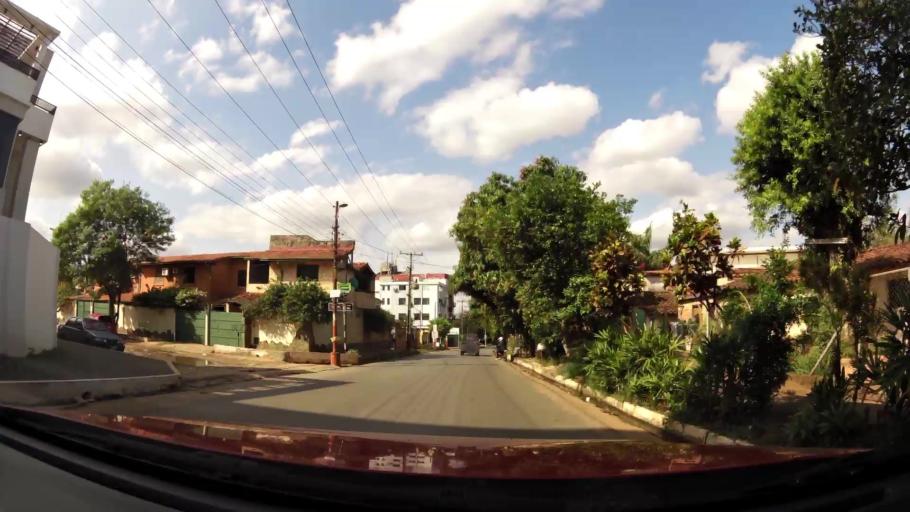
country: PY
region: Central
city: Fernando de la Mora
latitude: -25.3134
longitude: -57.5337
